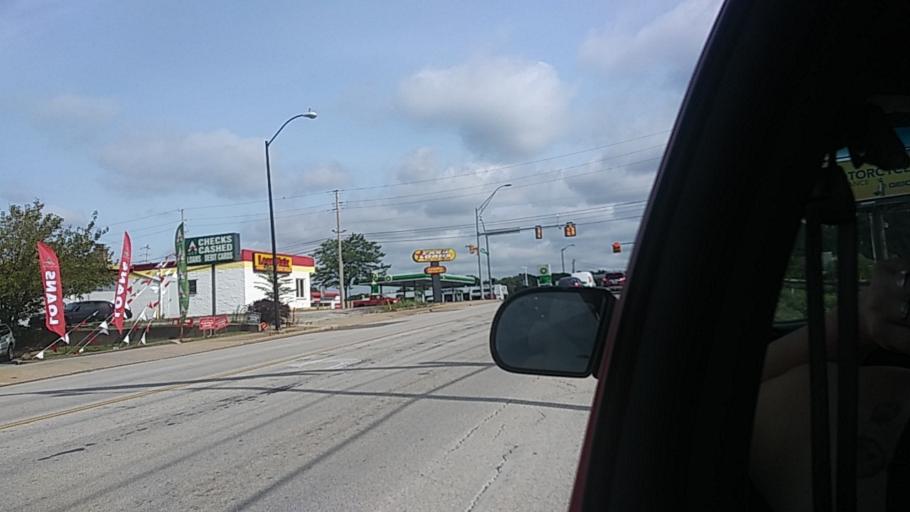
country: US
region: Ohio
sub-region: Summit County
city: Tallmadge
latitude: 41.1011
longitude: -81.4662
